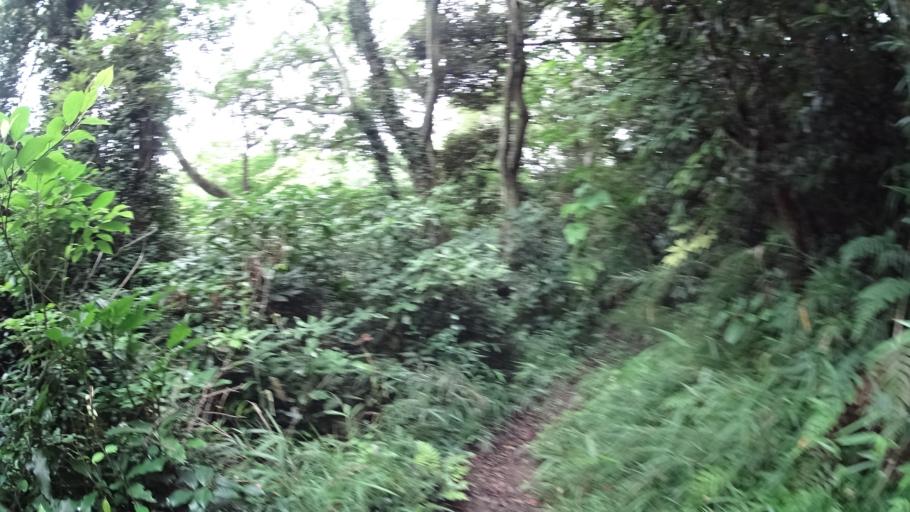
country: JP
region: Kanagawa
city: Yokosuka
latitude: 35.2525
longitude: 139.6334
